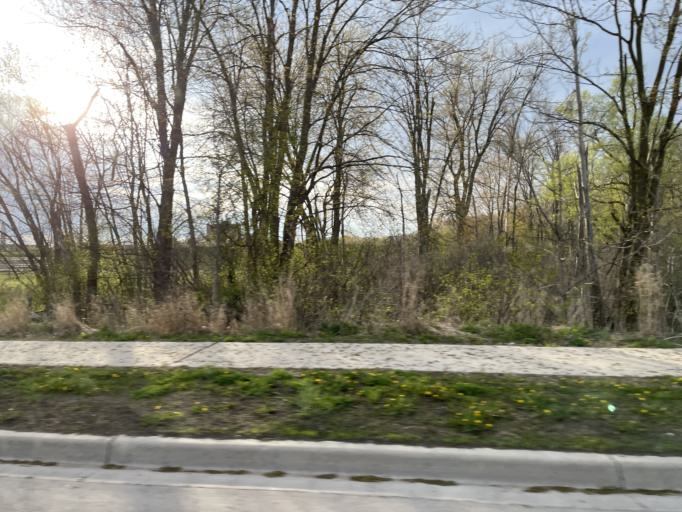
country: CA
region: Ontario
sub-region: Wellington County
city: Guelph
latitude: 43.5331
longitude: -80.2162
